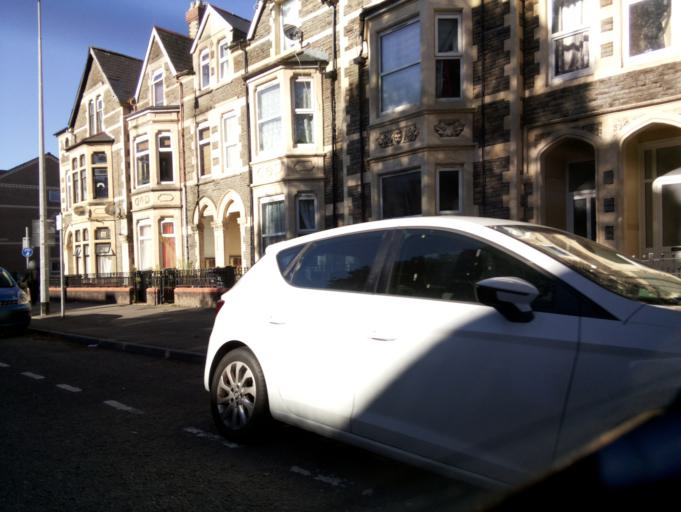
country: GB
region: Wales
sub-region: Cardiff
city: Cardiff
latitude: 51.4797
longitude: -3.1901
